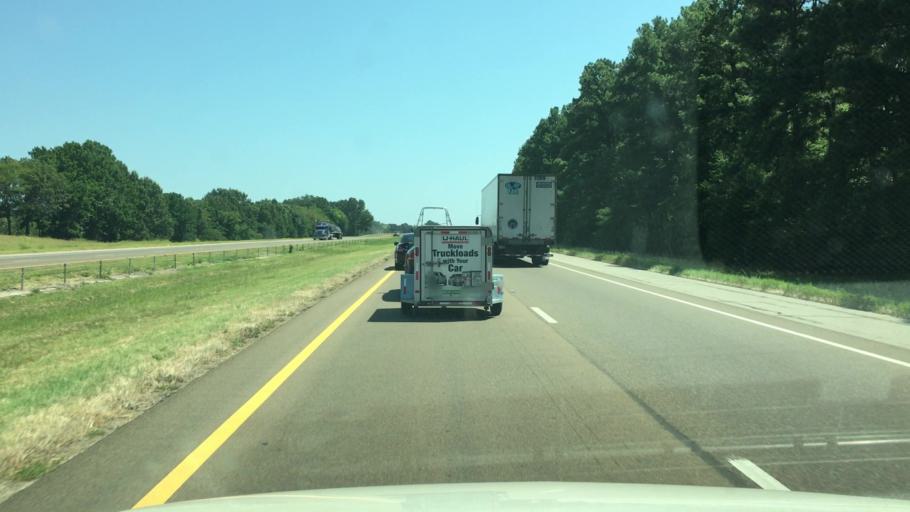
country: US
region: Texas
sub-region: Titus County
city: Mount Pleasant
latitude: 33.2315
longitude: -94.8820
